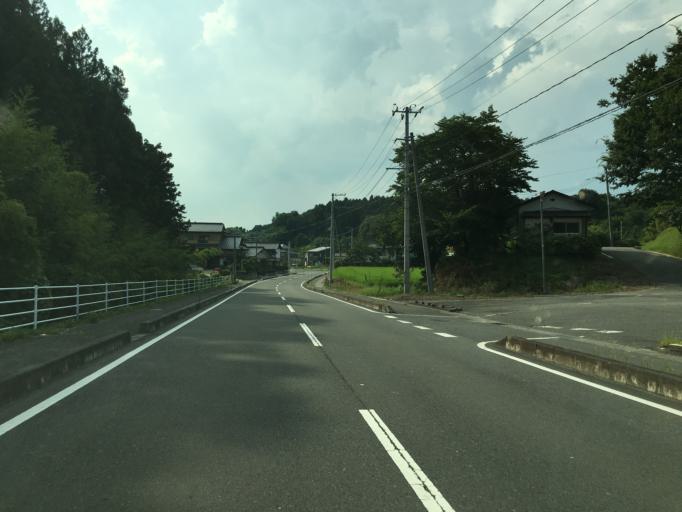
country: JP
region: Fukushima
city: Miharu
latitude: 37.4453
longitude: 140.4370
